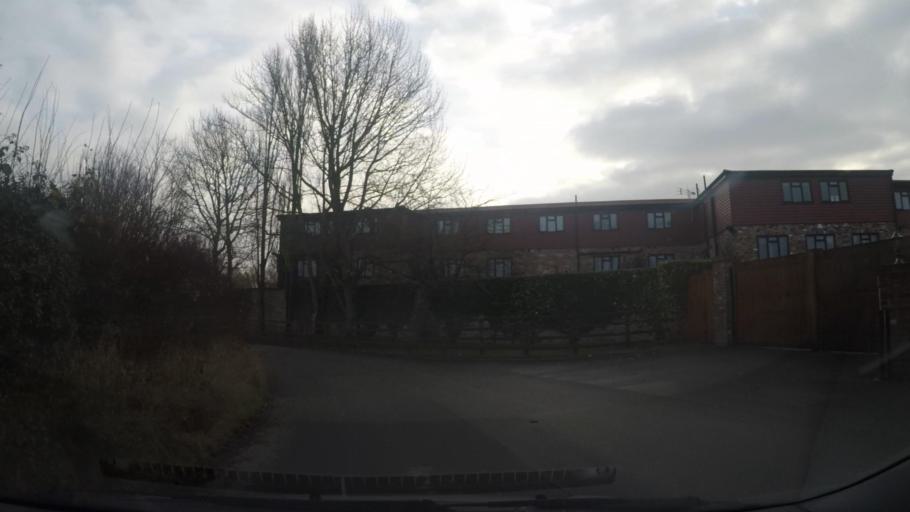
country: GB
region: England
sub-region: City and Borough of Leeds
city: Walton
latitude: 54.0285
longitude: -1.2923
